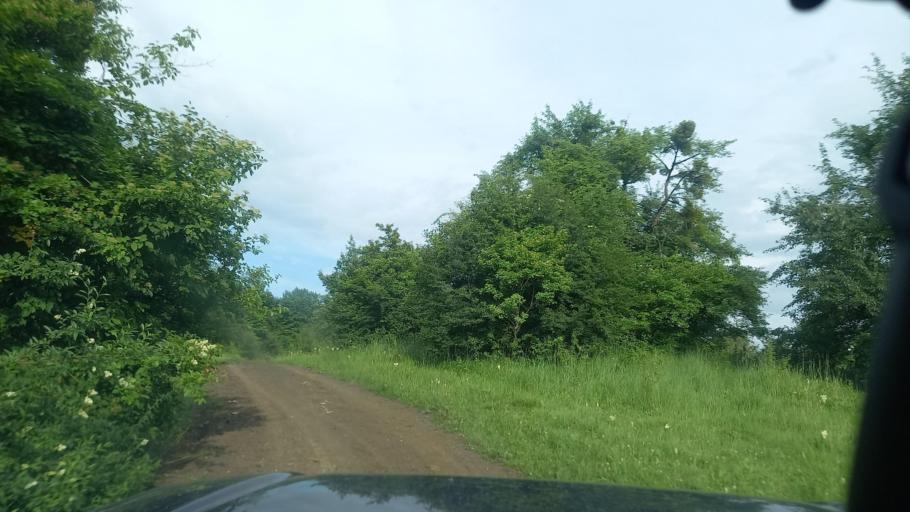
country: RU
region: Karachayevo-Cherkesiya
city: Kurdzhinovo
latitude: 44.1265
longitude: 41.0732
